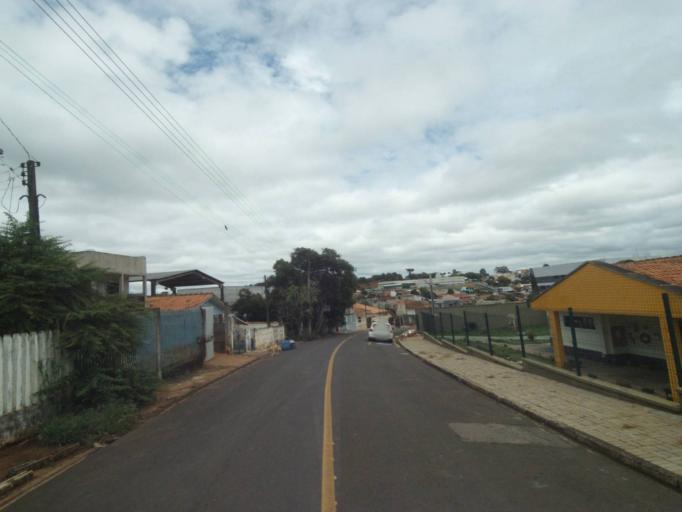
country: BR
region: Parana
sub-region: Telemaco Borba
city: Telemaco Borba
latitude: -24.3343
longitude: -50.6352
